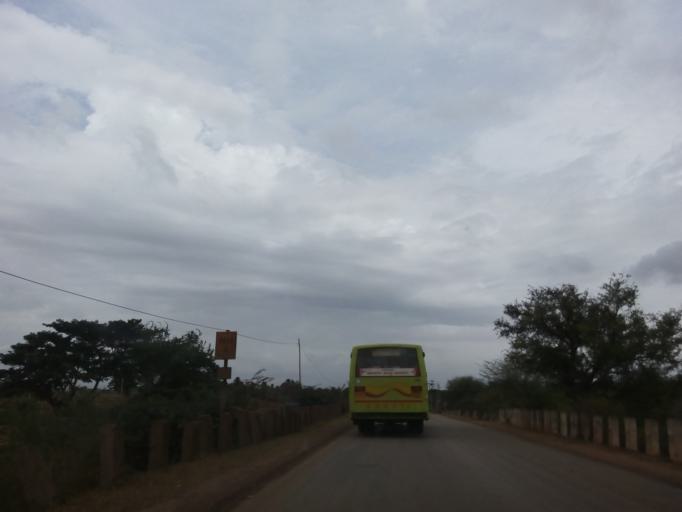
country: IN
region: Karnataka
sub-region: Davanagere
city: Harihar
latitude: 14.5117
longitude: 75.7836
